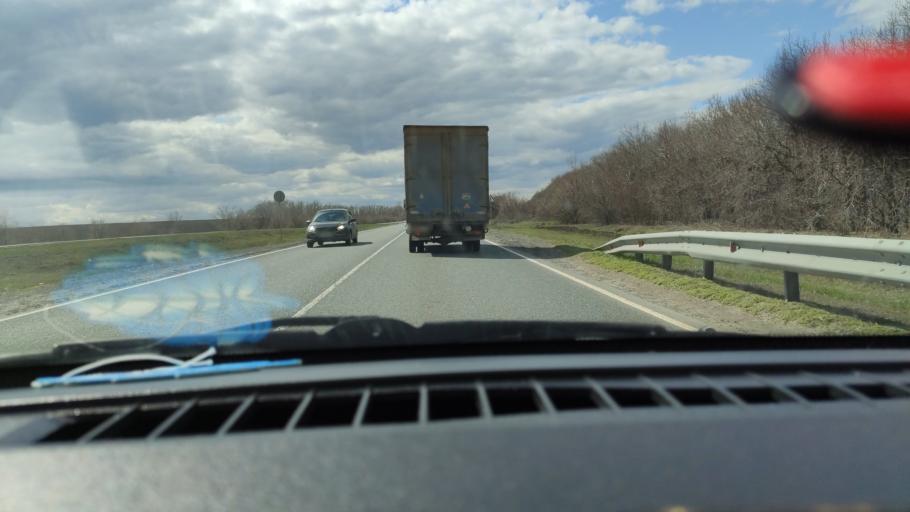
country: RU
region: Saratov
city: Balakovo
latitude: 52.1056
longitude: 47.7425
